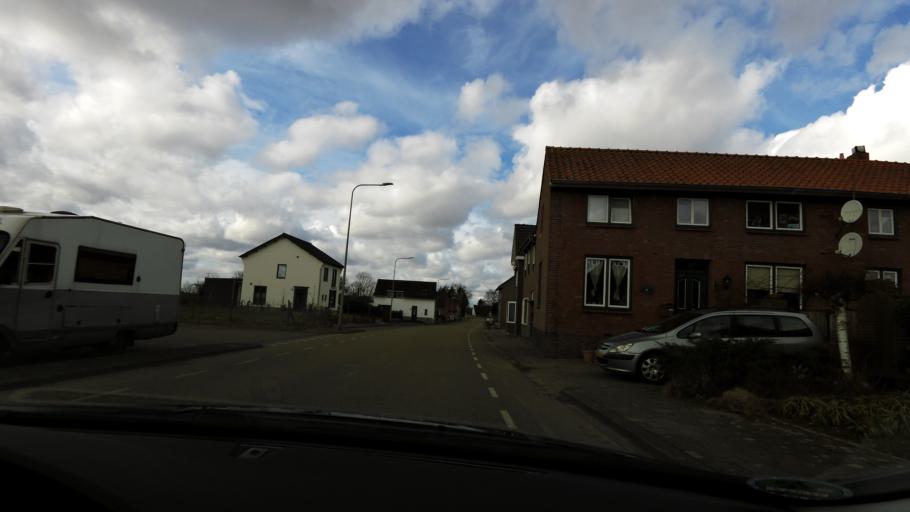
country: NL
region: Limburg
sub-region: Valkenburg aan de Geul
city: Broekhem
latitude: 50.8909
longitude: 5.8153
